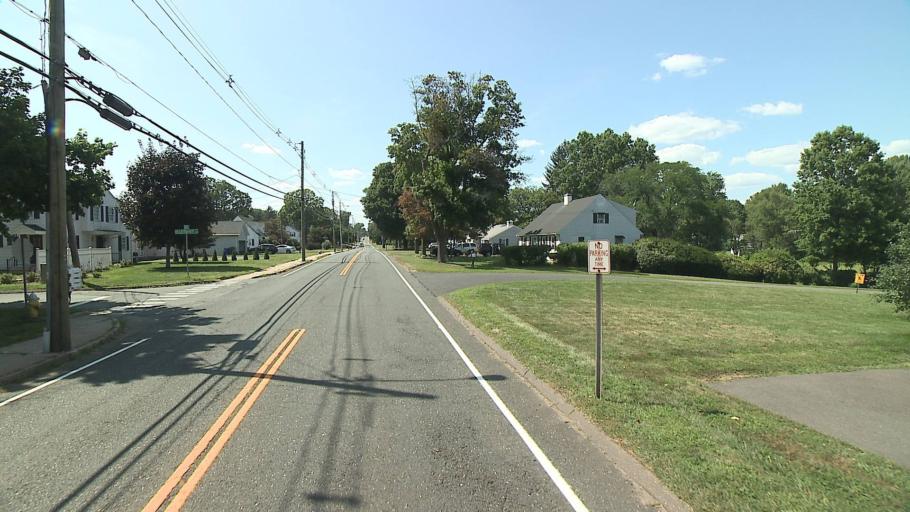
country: US
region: Connecticut
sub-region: Hartford County
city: Windsor Locks
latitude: 41.9261
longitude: -72.6382
